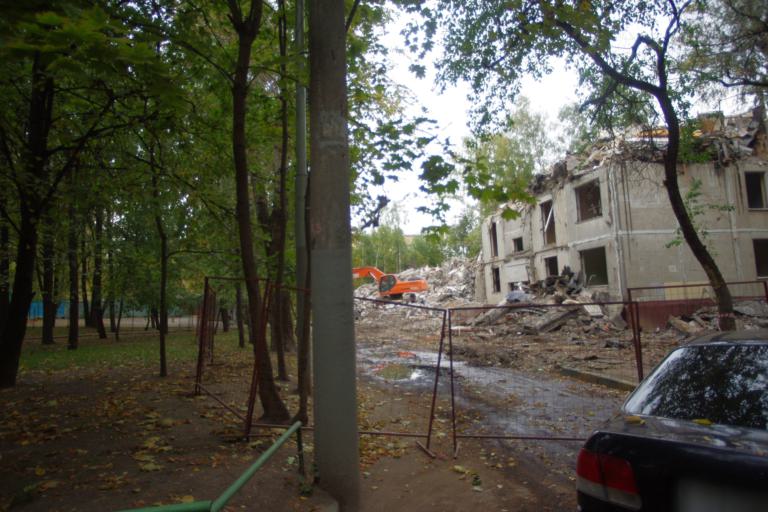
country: RU
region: Moskovskaya
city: Semenovskoye
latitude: 55.6893
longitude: 37.5566
